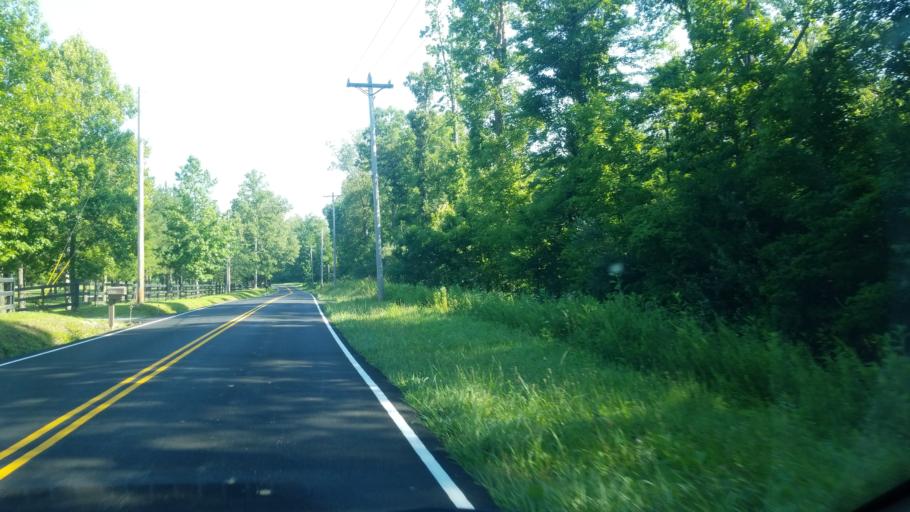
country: US
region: Tennessee
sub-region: Loudon County
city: Loudon
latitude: 35.7973
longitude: -84.3635
